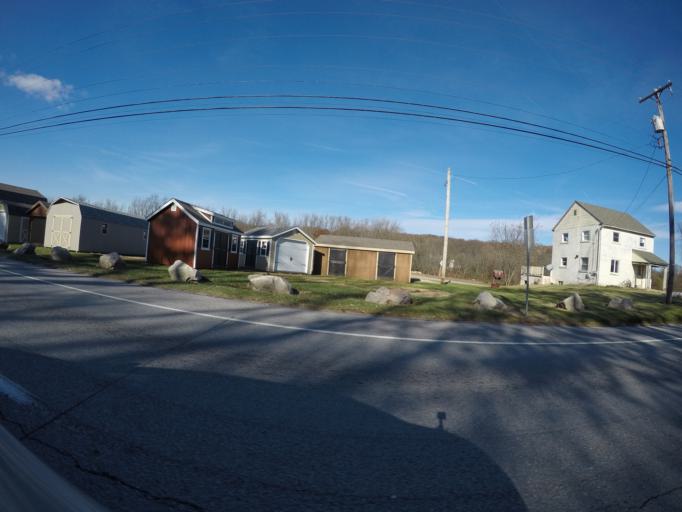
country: US
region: Pennsylvania
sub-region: Chester County
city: Parkesburg
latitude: 39.9832
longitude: -75.9293
